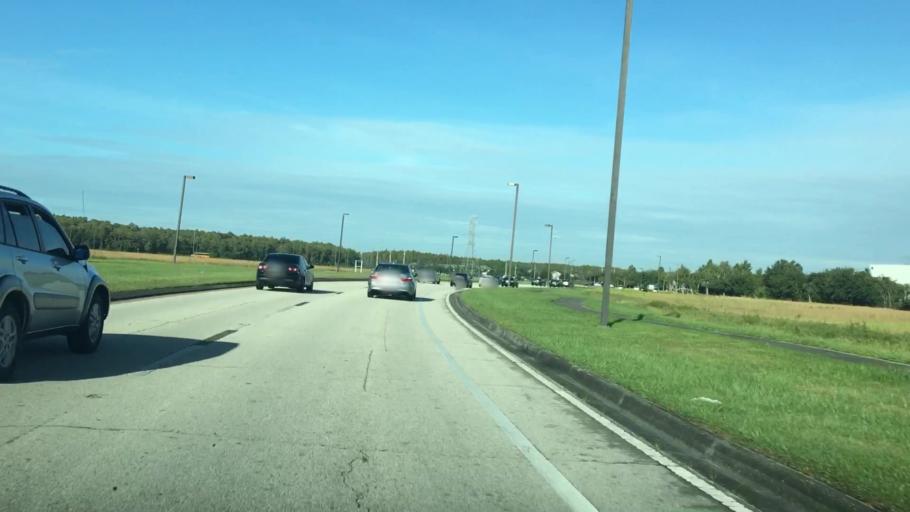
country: US
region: Florida
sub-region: Orange County
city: Conway
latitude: 28.4647
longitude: -81.2838
